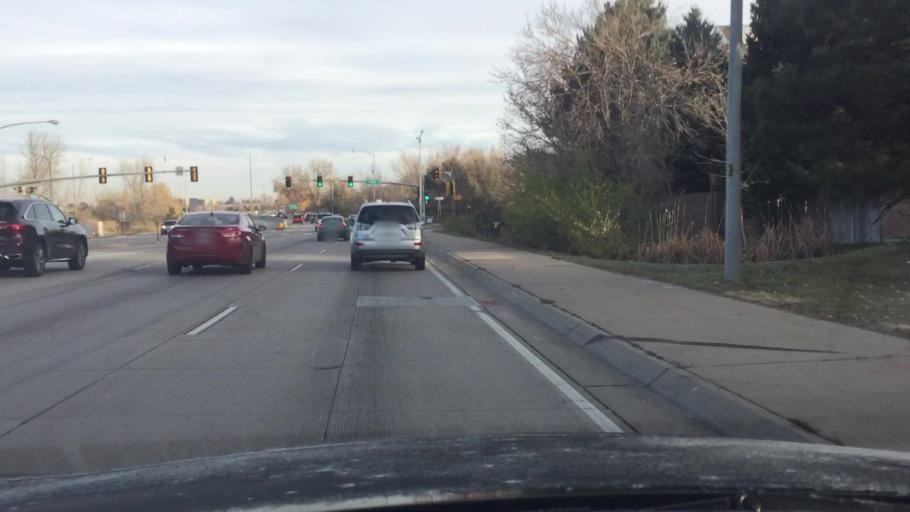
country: US
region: Colorado
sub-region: Arapahoe County
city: Dove Valley
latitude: 39.6465
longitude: -104.8287
